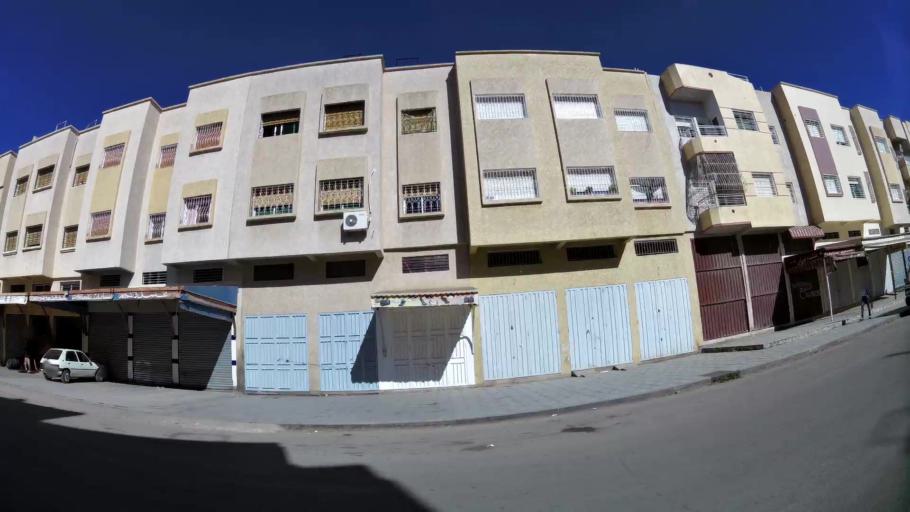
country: MA
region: Fes-Boulemane
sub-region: Fes
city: Fes
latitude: 34.0166
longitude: -4.9657
